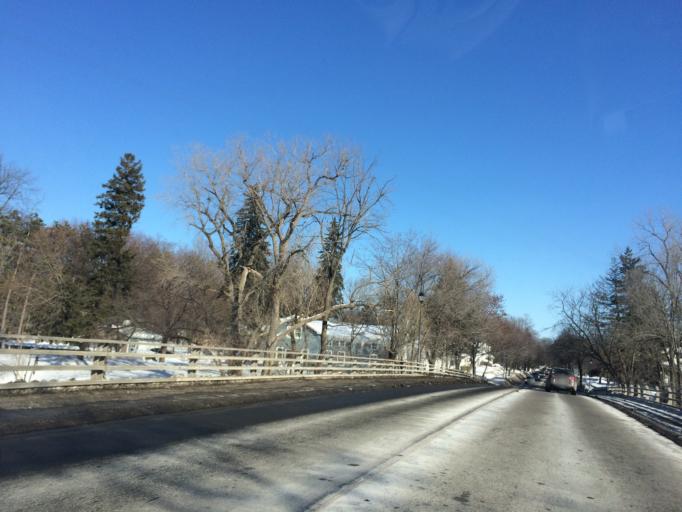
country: US
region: New York
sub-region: Monroe County
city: Fairport
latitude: 43.1001
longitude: -77.4566
